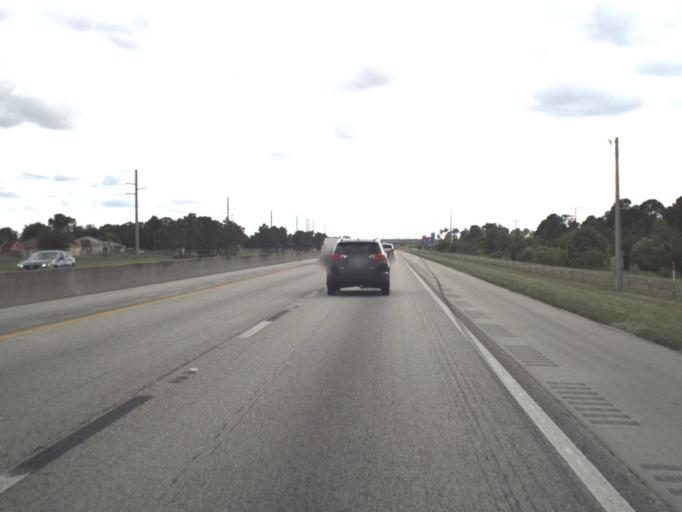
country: US
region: Florida
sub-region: Saint Lucie County
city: River Park
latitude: 27.3258
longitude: -80.3744
